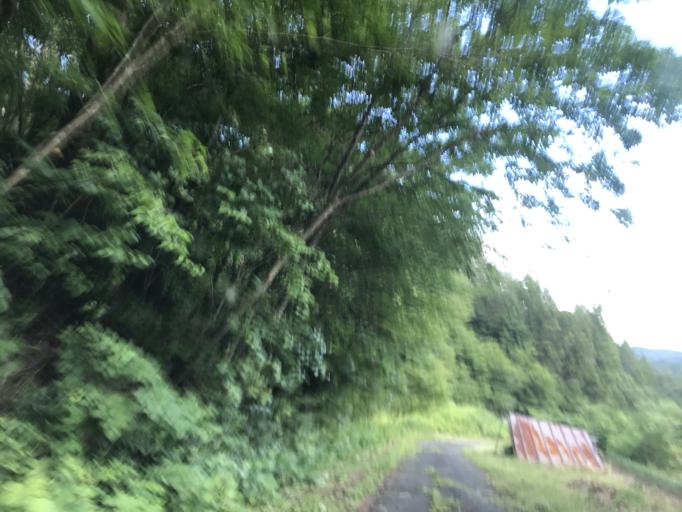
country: JP
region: Iwate
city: Ichinoseki
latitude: 38.8963
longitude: 140.9518
